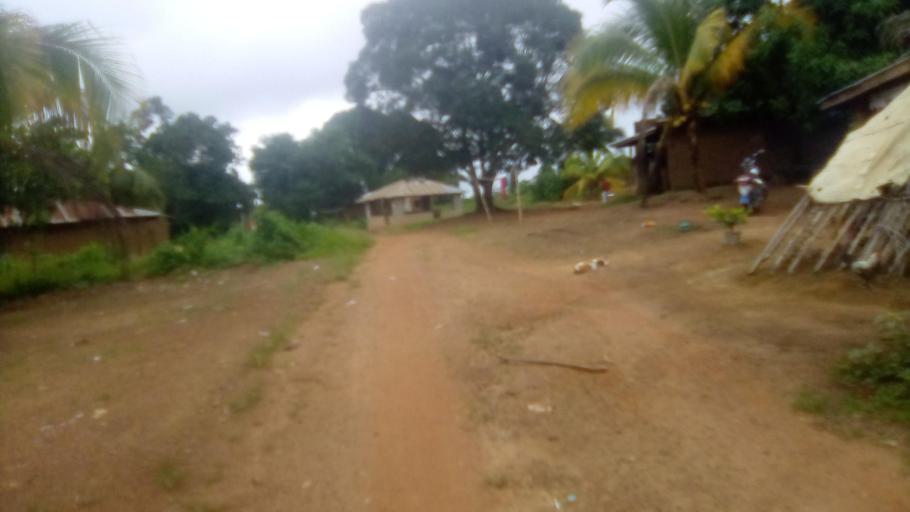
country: SL
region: Eastern Province
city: Kailahun
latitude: 8.3066
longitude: -10.5600
